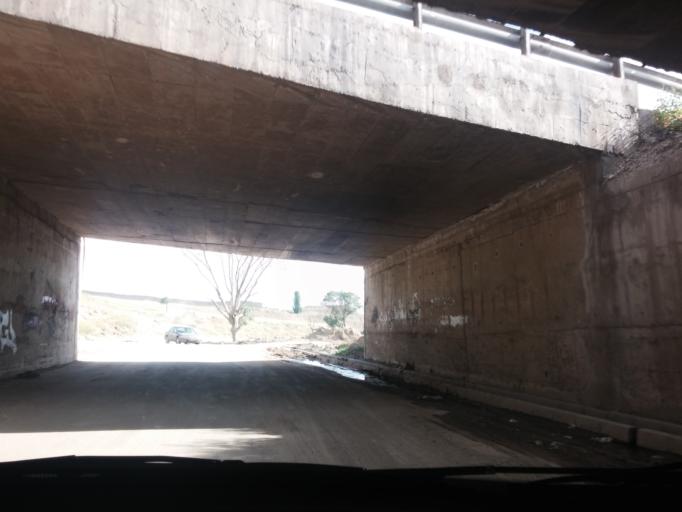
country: IR
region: Tehran
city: Damavand
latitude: 35.7201
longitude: 51.8987
